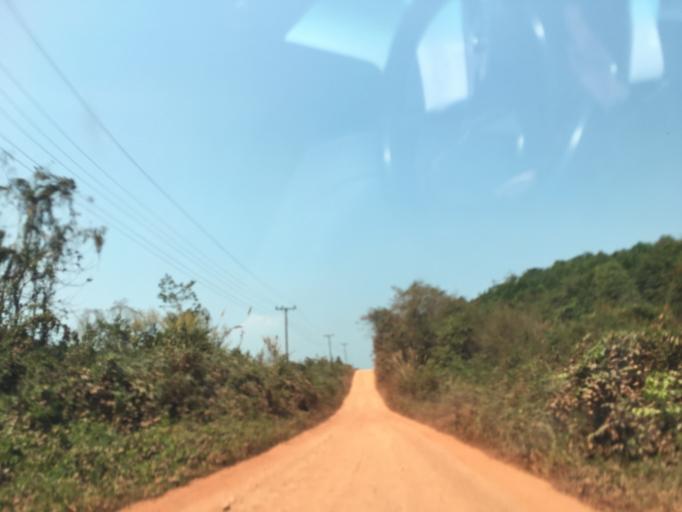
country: LA
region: Bolikhamxai
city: Bolikhan
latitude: 18.7339
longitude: 103.6298
